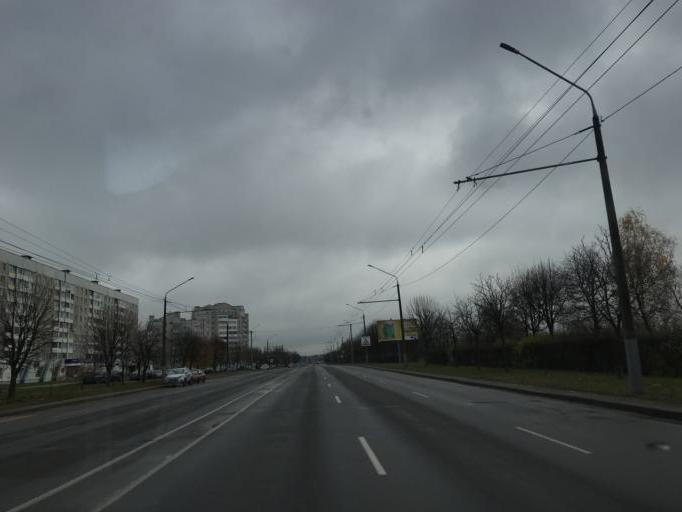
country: BY
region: Mogilev
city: Mahilyow
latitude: 53.8671
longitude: 30.3290
